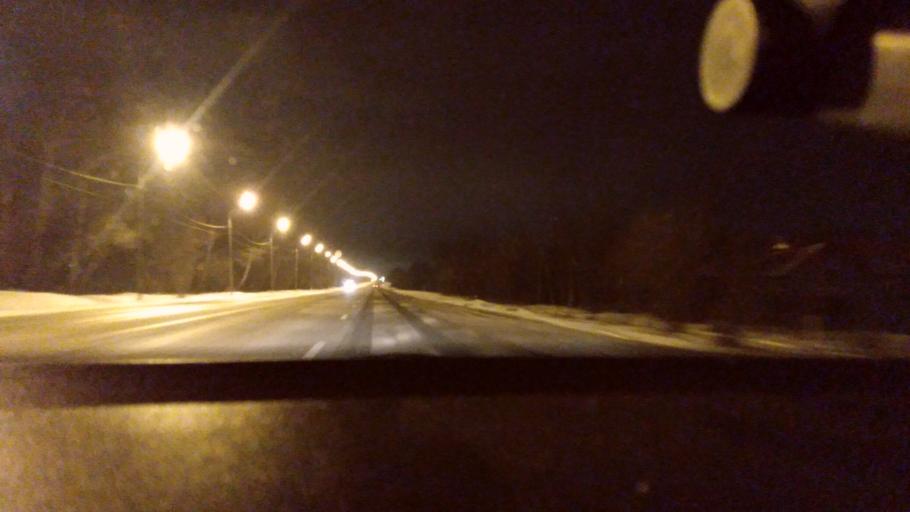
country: RU
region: Moskovskaya
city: Beloozerskiy
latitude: 55.3732
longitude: 38.3829
